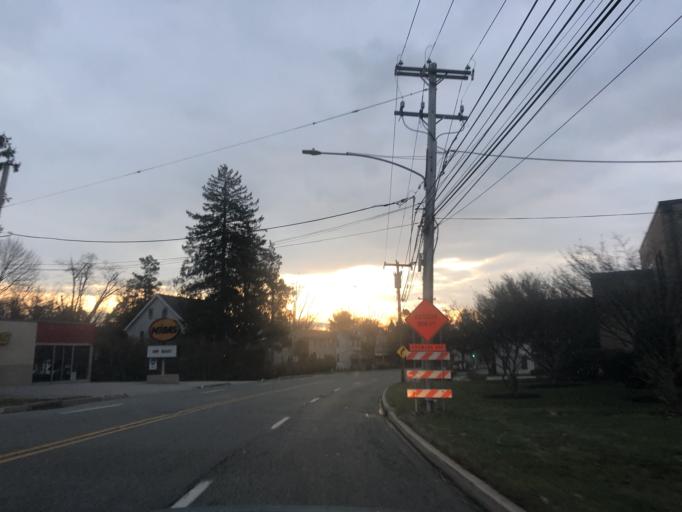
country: US
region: Pennsylvania
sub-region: Montgomery County
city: Bryn Mawr
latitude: 40.0128
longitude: -75.3166
